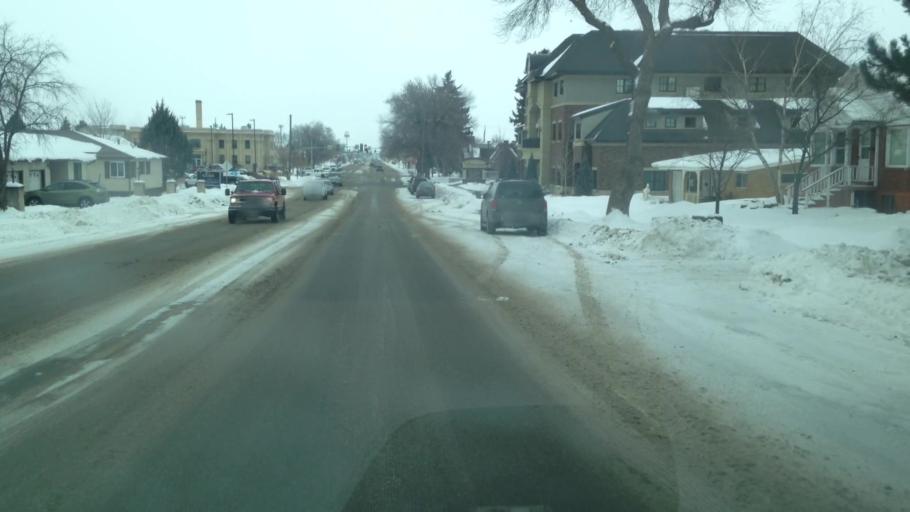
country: US
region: Idaho
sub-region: Madison County
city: Rexburg
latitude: 43.8242
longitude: -111.7781
